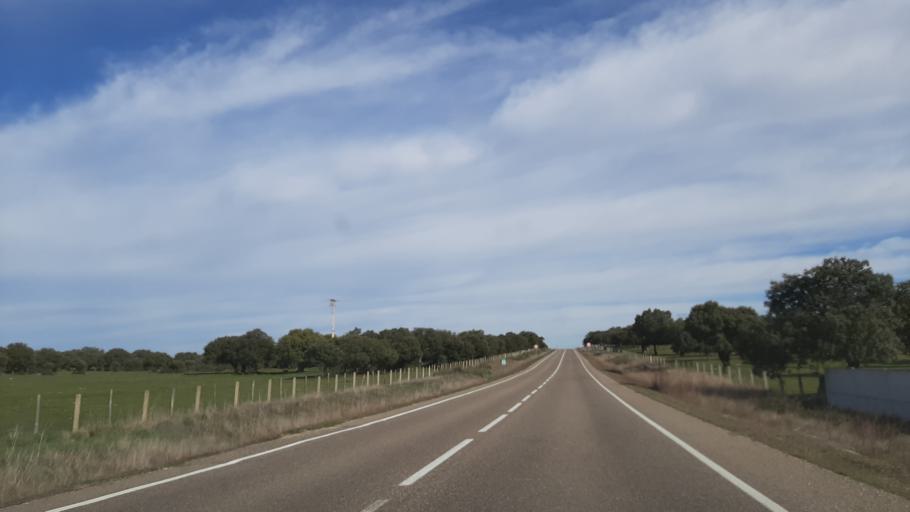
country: ES
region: Castille and Leon
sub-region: Provincia de Salamanca
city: Ledesma
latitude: 41.0898
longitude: -5.9557
